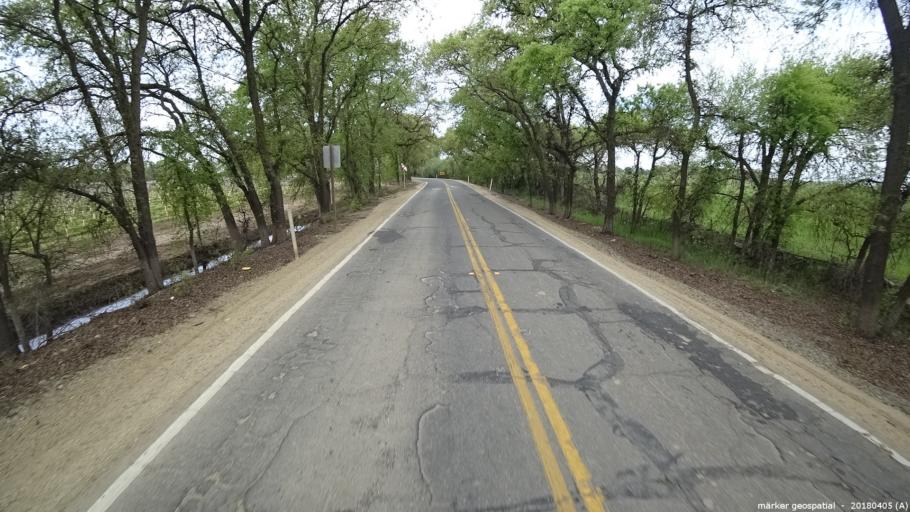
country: US
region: California
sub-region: San Joaquin County
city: Thornton
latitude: 38.2399
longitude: -121.4165
